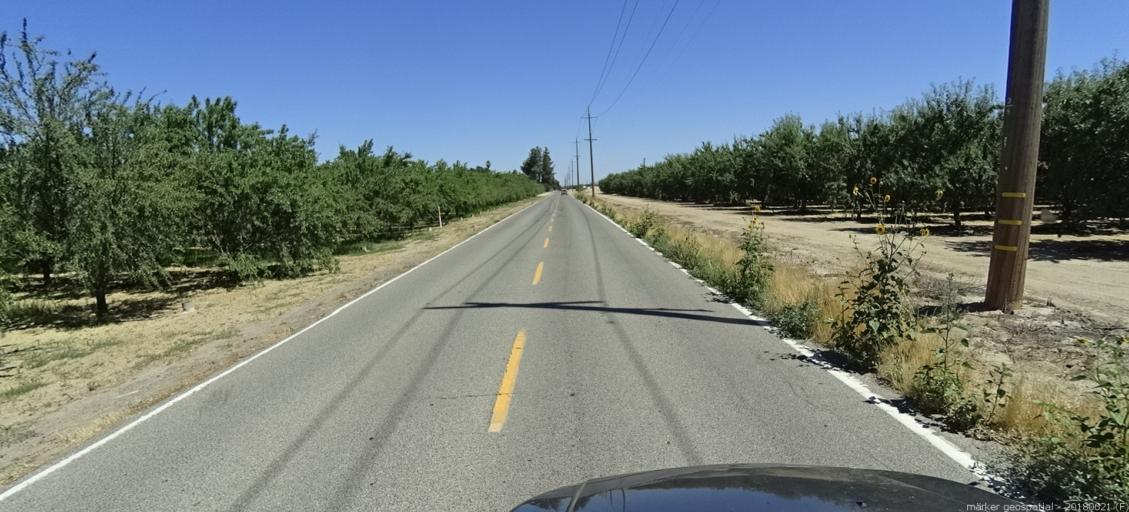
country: US
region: California
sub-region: Madera County
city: Bonadelle Ranchos-Madera Ranchos
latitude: 36.8712
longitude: -119.9113
